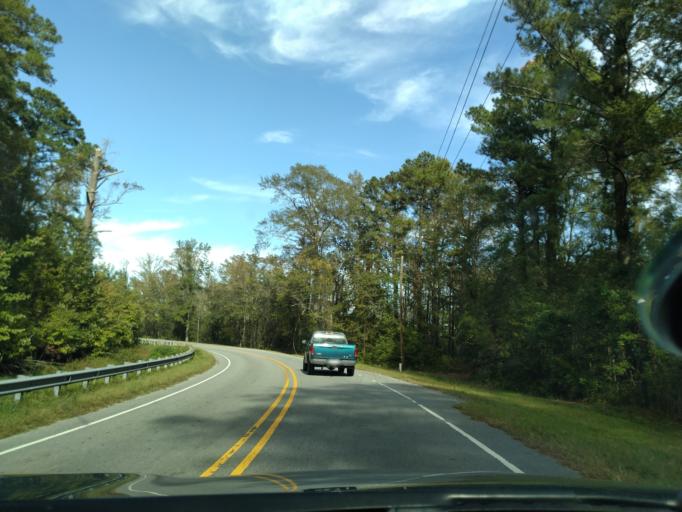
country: US
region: North Carolina
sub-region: Beaufort County
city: Belhaven
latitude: 35.6332
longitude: -76.6126
